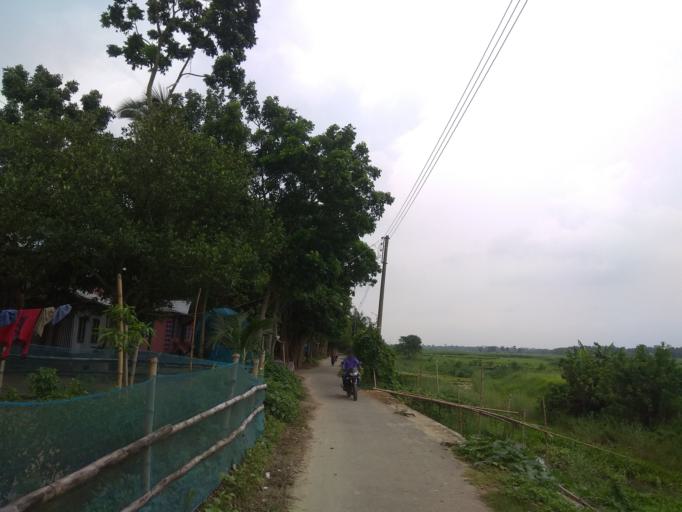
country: BD
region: Dhaka
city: Dohar
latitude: 23.4883
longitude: 90.0326
